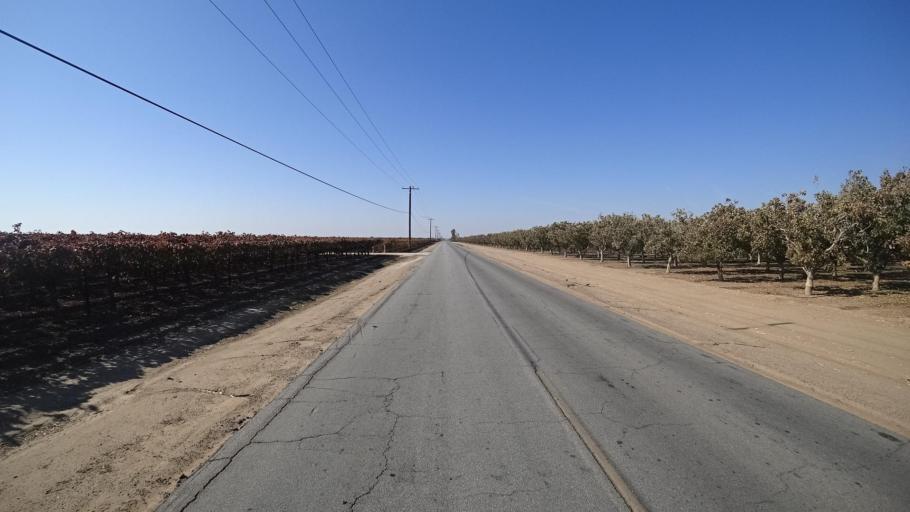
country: US
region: California
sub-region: Kern County
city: McFarland
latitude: 35.7178
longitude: -119.1911
